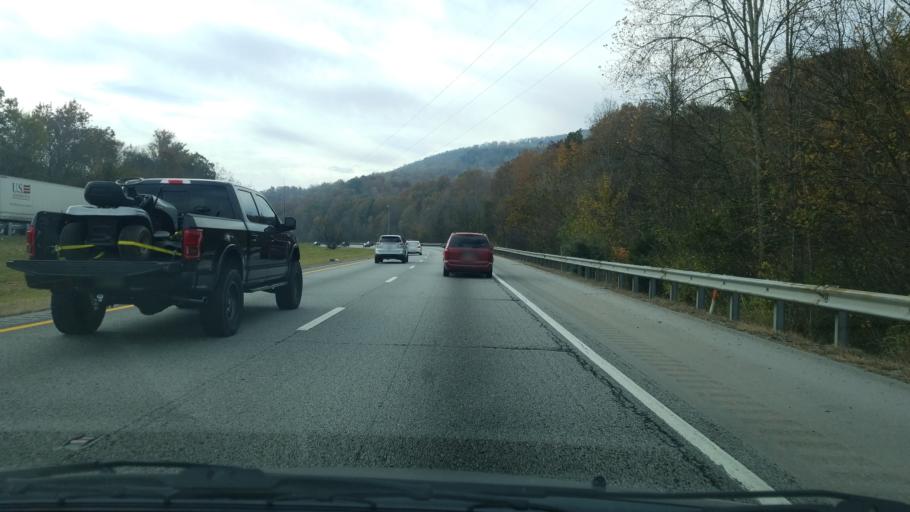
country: US
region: Tennessee
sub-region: Hamilton County
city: Lookout Mountain
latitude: 35.0083
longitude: -85.3937
